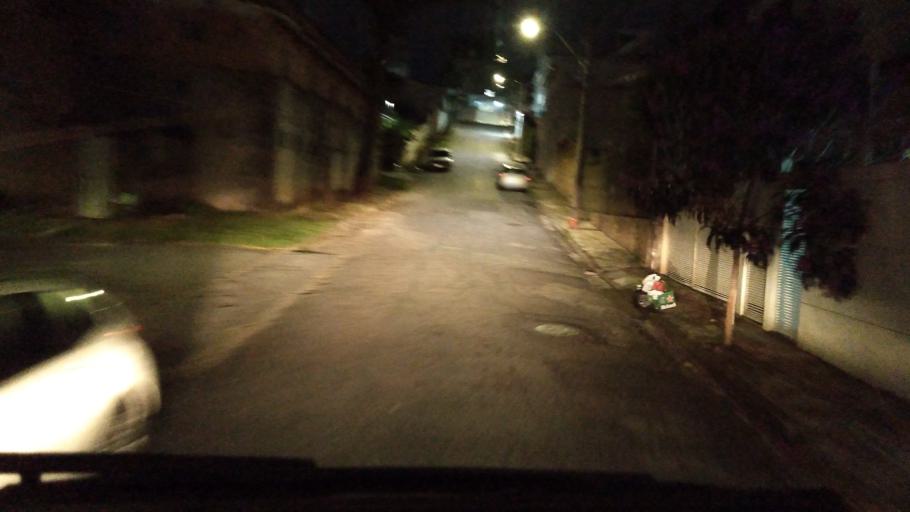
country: BR
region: Minas Gerais
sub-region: Belo Horizonte
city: Belo Horizonte
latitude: -19.8988
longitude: -43.9731
